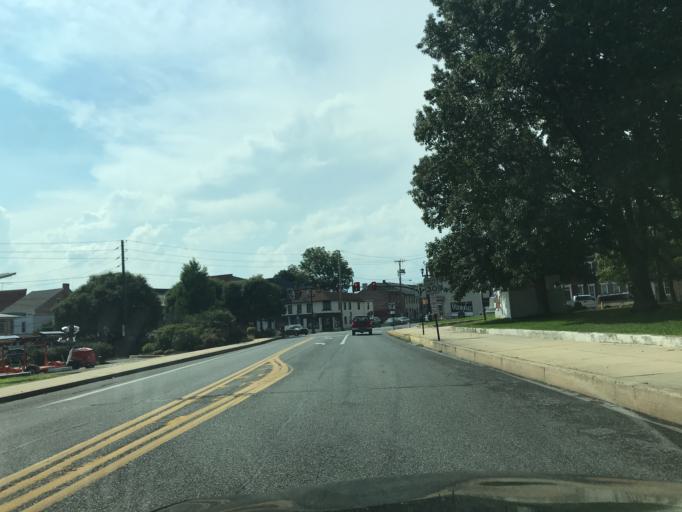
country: US
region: Pennsylvania
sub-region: Lancaster County
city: Columbia
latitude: 40.0335
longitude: -76.4986
